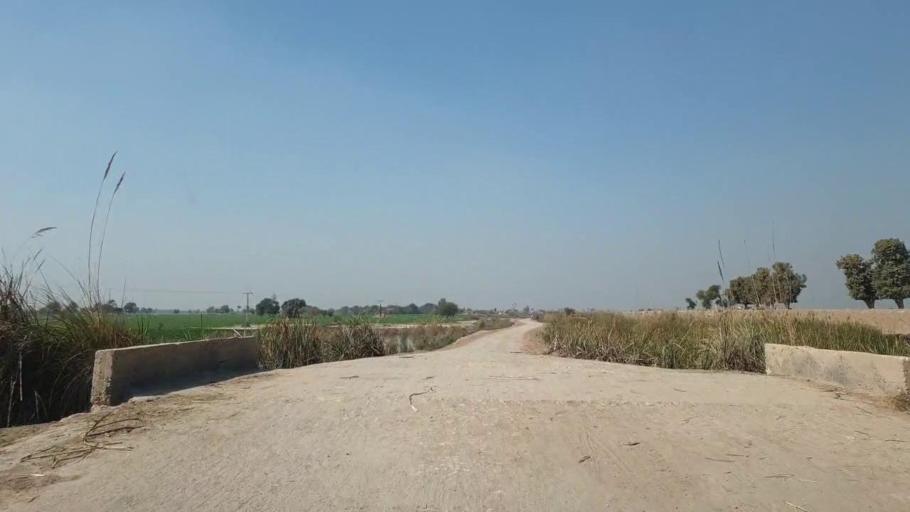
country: PK
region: Sindh
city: Bhit Shah
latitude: 25.9210
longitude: 68.4934
